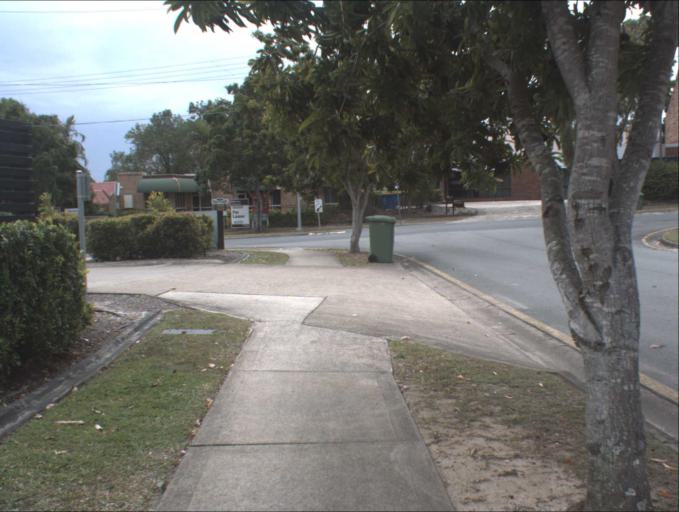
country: AU
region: Queensland
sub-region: Logan
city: Springwood
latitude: -27.6155
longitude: 153.1269
